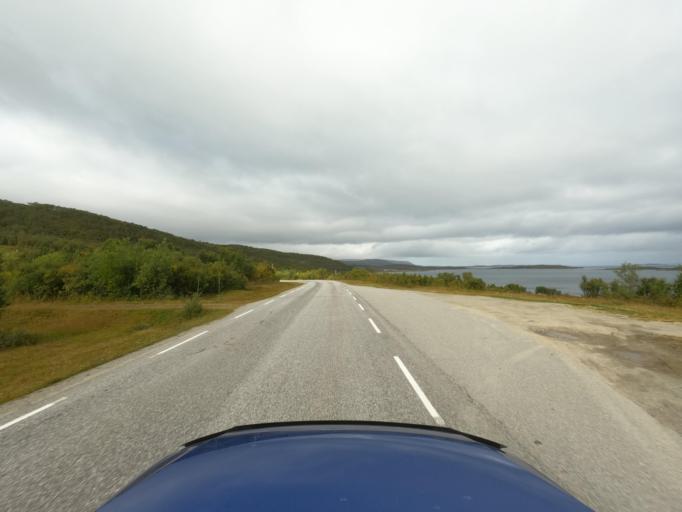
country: NO
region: Finnmark Fylke
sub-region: Porsanger
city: Lakselv
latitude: 70.3295
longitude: 25.0713
